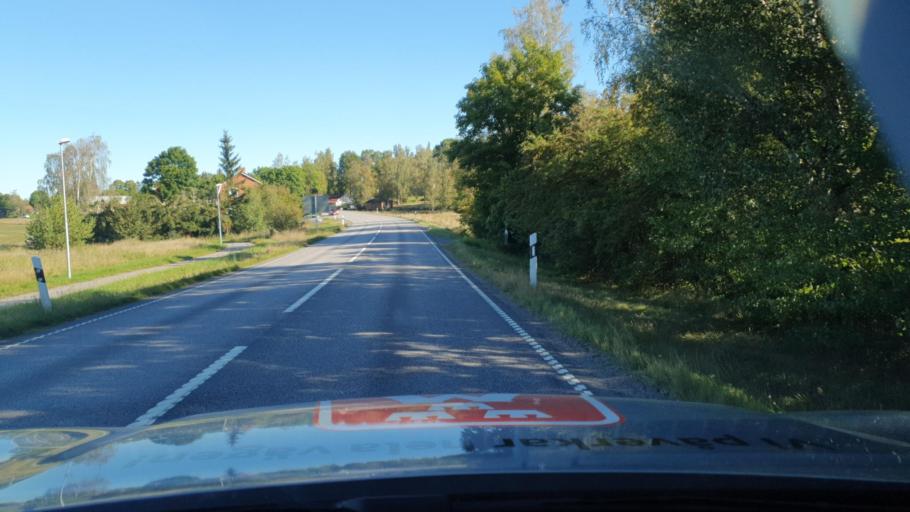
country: SE
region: OEstergoetland
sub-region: Finspangs Kommun
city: Finspang
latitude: 58.7357
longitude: 15.5771
